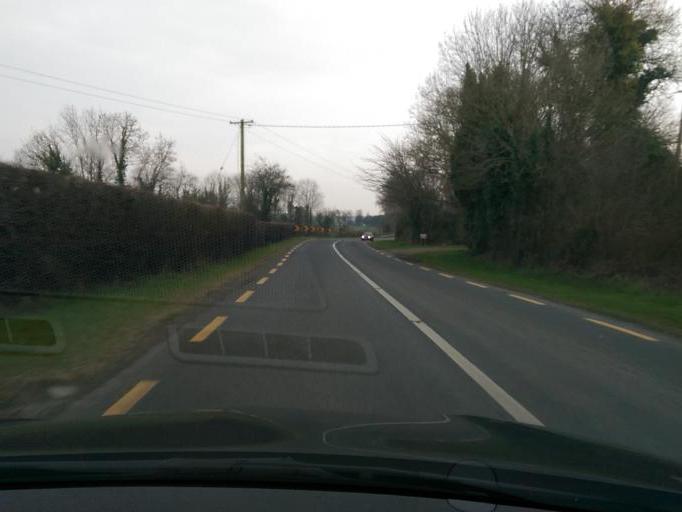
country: IE
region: Leinster
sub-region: An Longfort
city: Ballymahon
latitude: 53.5273
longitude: -7.7943
